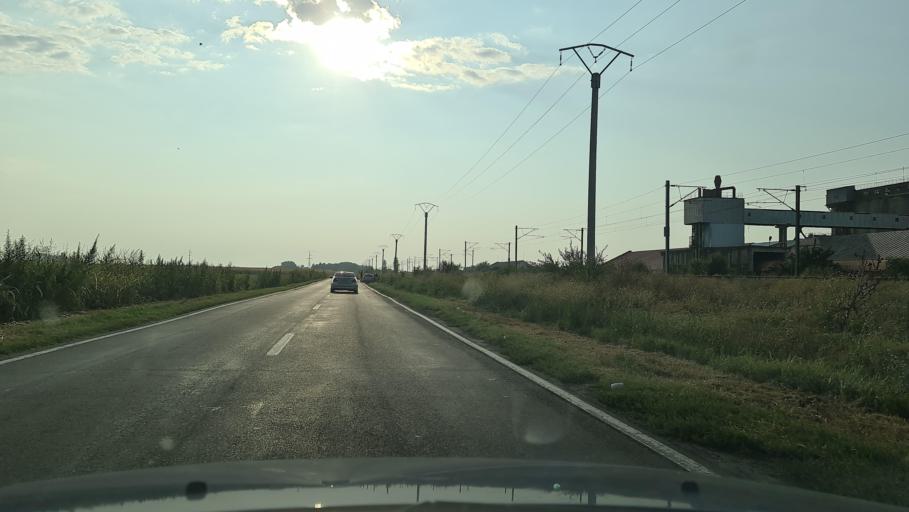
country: RO
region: Calarasi
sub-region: Oras Lehliu Gara
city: Razvani
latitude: 44.4374
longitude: 26.8750
